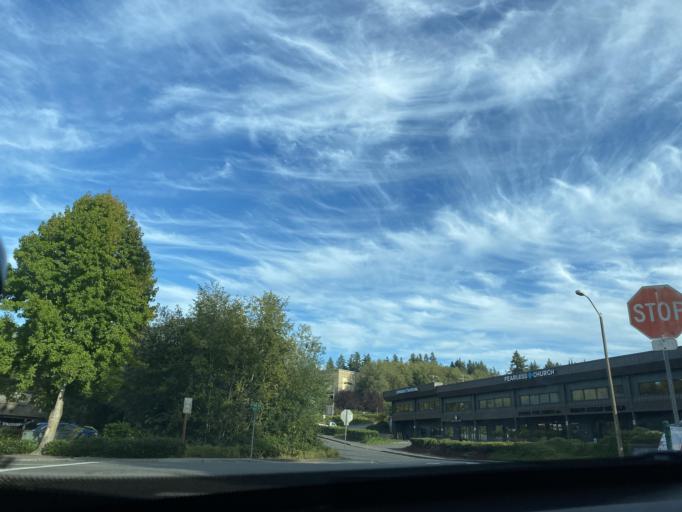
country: US
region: Washington
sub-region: Kitsap County
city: Poulsbo
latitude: 47.7390
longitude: -122.6406
